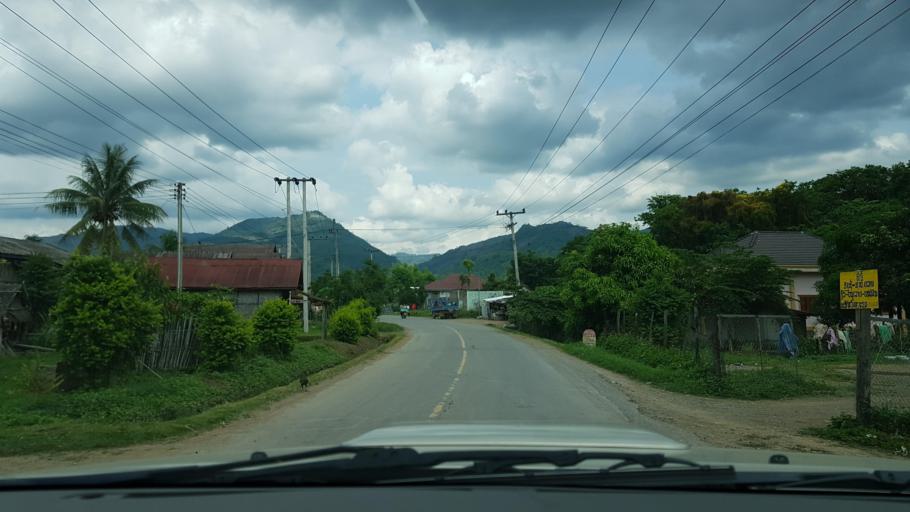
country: LA
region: Loungnamtha
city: Muang Nale
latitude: 20.1527
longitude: 101.4860
